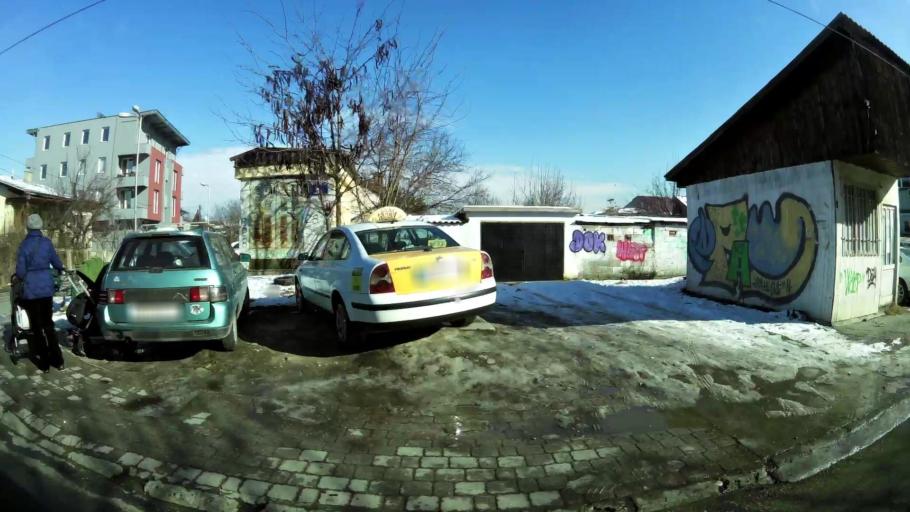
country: MK
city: Krushopek
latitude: 42.0102
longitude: 21.3746
